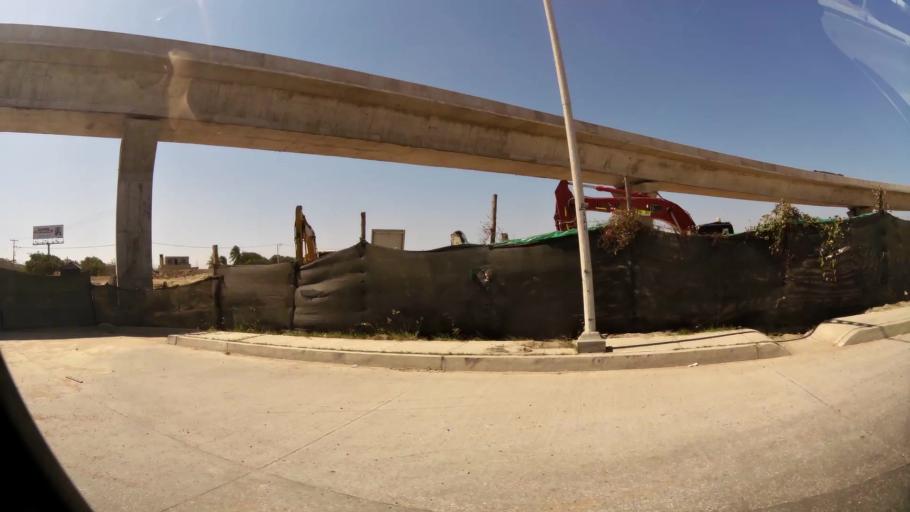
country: CO
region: Atlantico
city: Barranquilla
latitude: 10.9515
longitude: -74.7672
